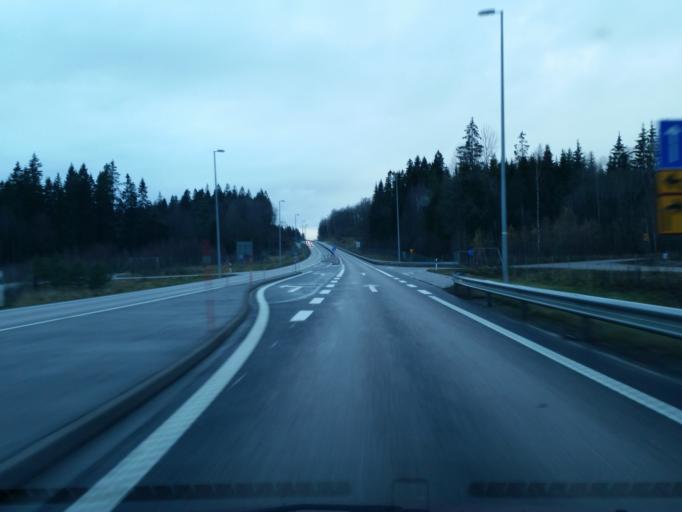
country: SE
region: Vaestra Goetaland
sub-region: Boras Kommun
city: Ganghester
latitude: 57.6743
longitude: 12.9941
